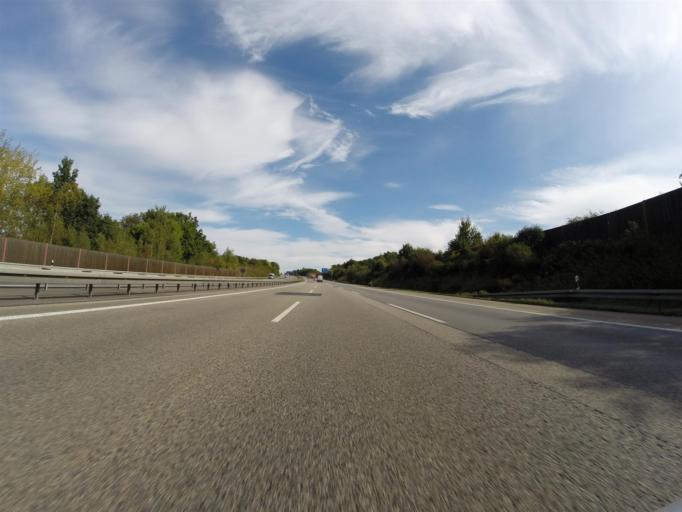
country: DE
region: Saxony
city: Frankenberg
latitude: 50.9190
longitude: 13.0331
